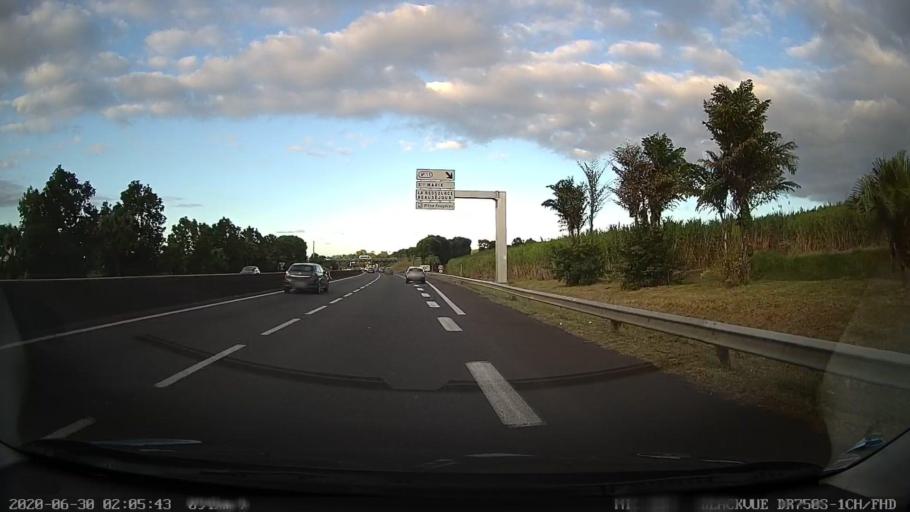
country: RE
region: Reunion
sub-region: Reunion
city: Sainte-Marie
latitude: -20.9037
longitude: 55.5410
